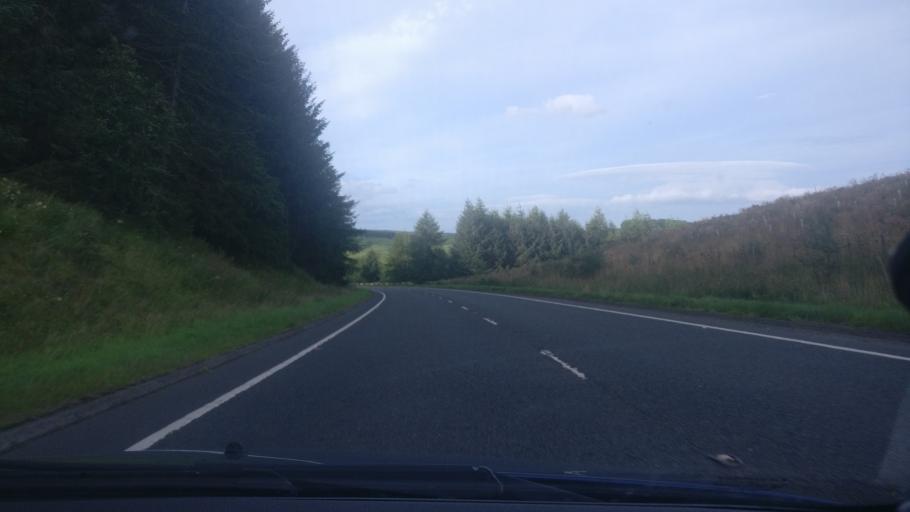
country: GB
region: Scotland
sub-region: The Scottish Borders
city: Selkirk
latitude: 55.5218
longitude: -2.8292
